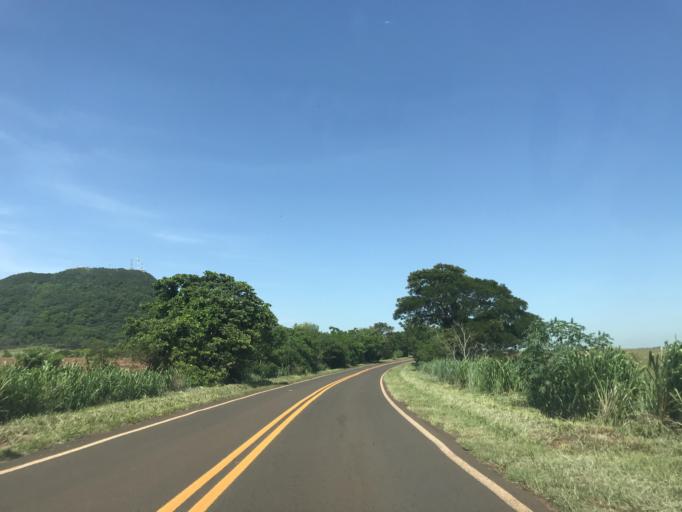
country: BR
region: Parana
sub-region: Terra Rica
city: Terra Rica
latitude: -22.7705
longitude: -52.6447
